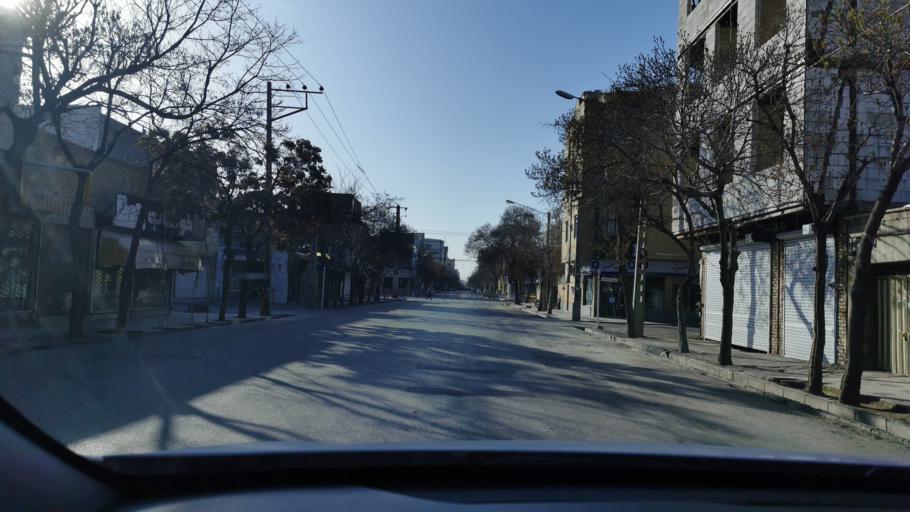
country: IR
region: Razavi Khorasan
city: Mashhad
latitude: 36.3008
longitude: 59.6341
